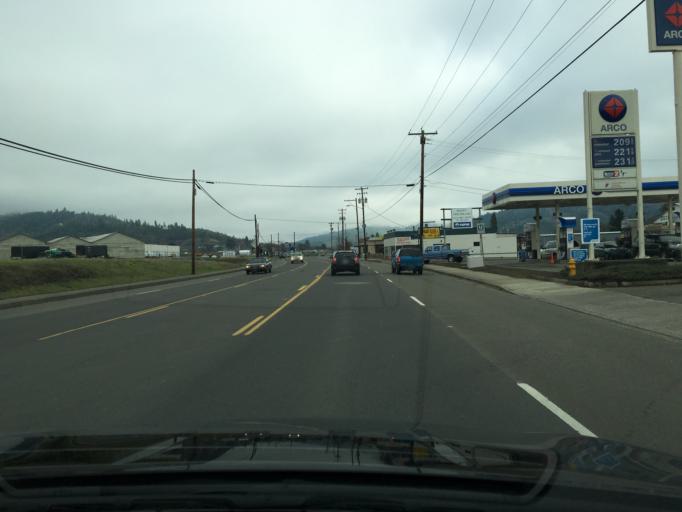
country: US
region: Oregon
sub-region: Douglas County
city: Roseburg
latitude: 43.2133
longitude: -123.3362
